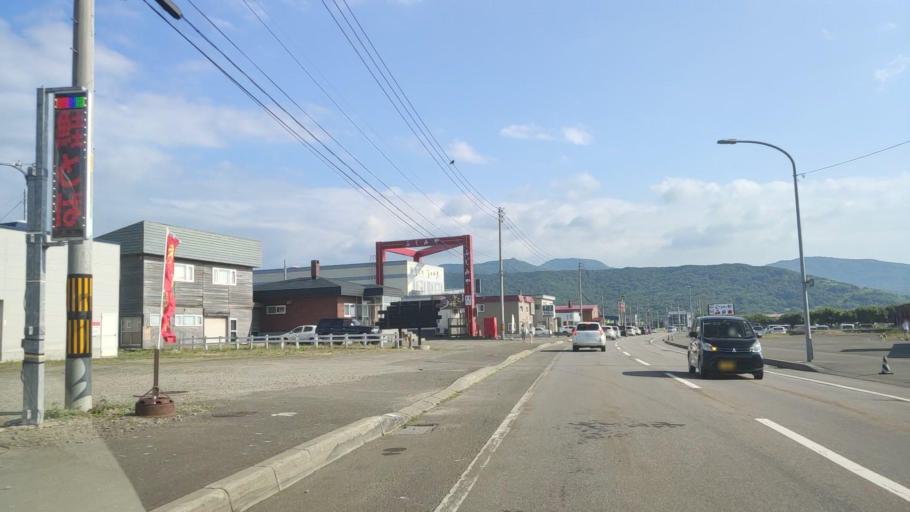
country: JP
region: Hokkaido
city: Ishikari
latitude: 43.5852
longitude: 141.3876
